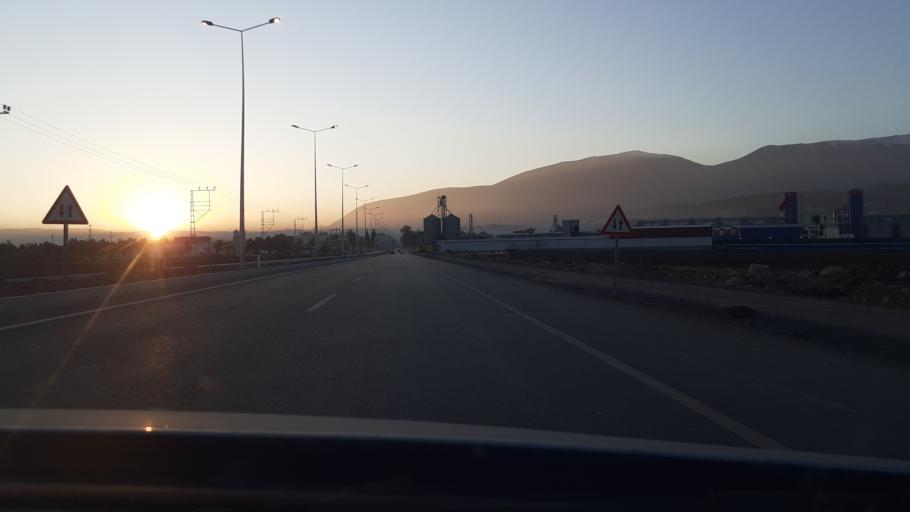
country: TR
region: Hatay
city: Kirikhan
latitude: 36.5014
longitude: 36.3846
